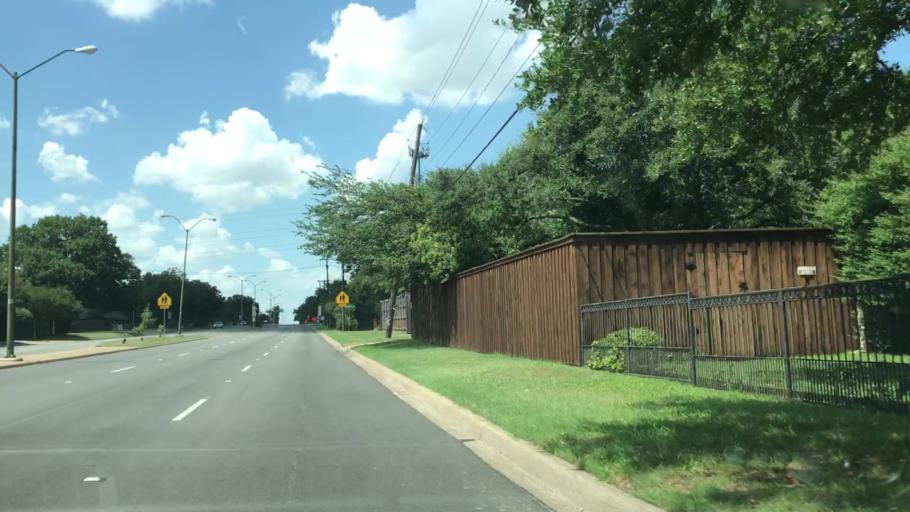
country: US
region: Texas
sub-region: Dallas County
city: University Park
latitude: 32.8984
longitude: -96.8382
